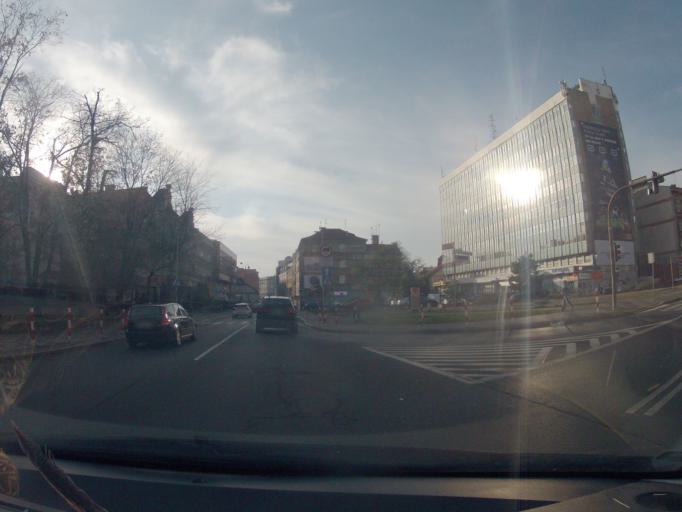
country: PL
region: Opole Voivodeship
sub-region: Powiat opolski
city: Opole
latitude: 50.6677
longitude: 17.9287
